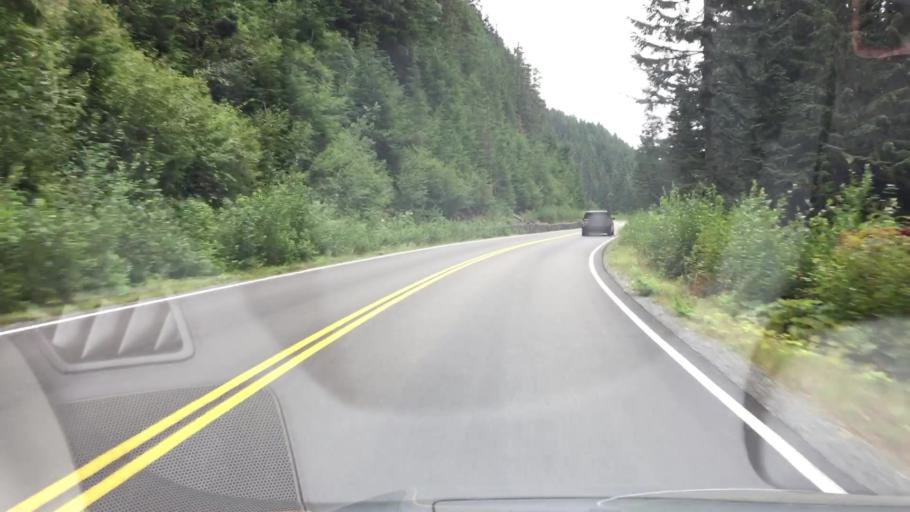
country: US
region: Washington
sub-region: Pierce County
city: Buckley
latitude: 46.7786
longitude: -121.7636
